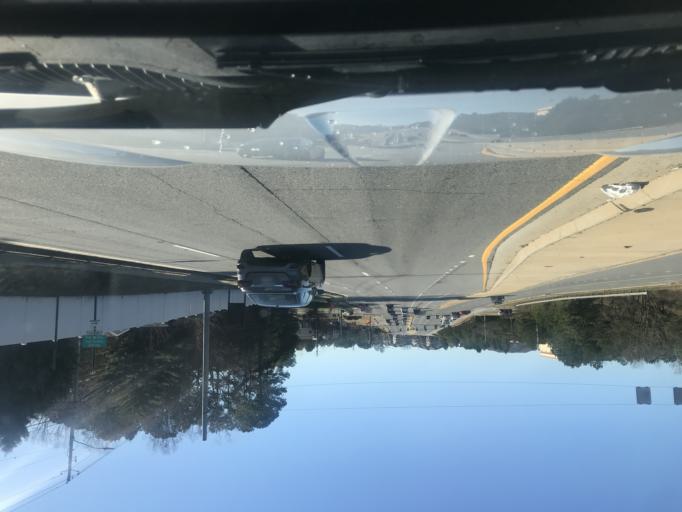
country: US
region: Georgia
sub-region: Gwinnett County
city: Duluth
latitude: 33.9766
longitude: -84.0855
